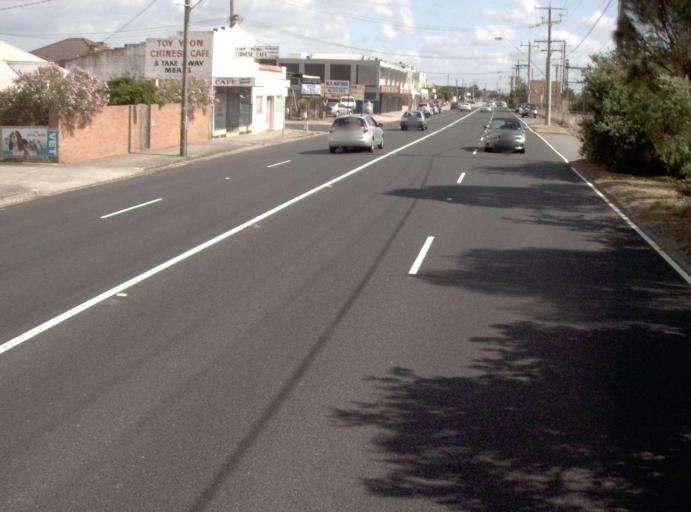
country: AU
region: Victoria
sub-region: Kingston
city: Bonbeach
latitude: -38.0591
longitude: 145.1187
